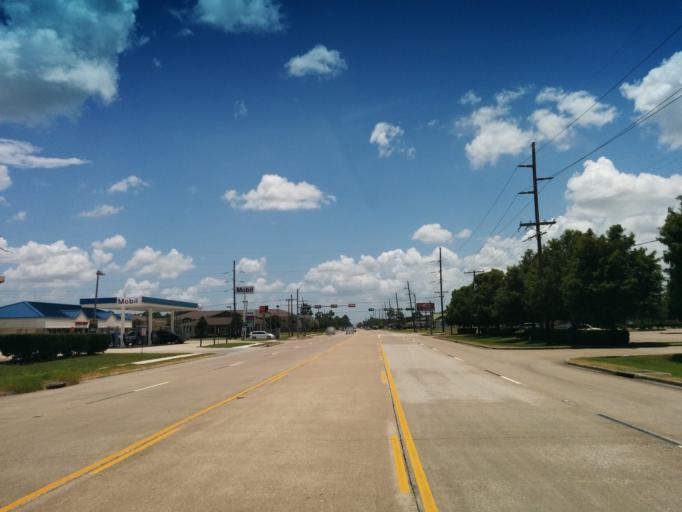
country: US
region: Texas
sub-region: Jefferson County
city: Beaumont
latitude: 30.0925
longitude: -94.1899
